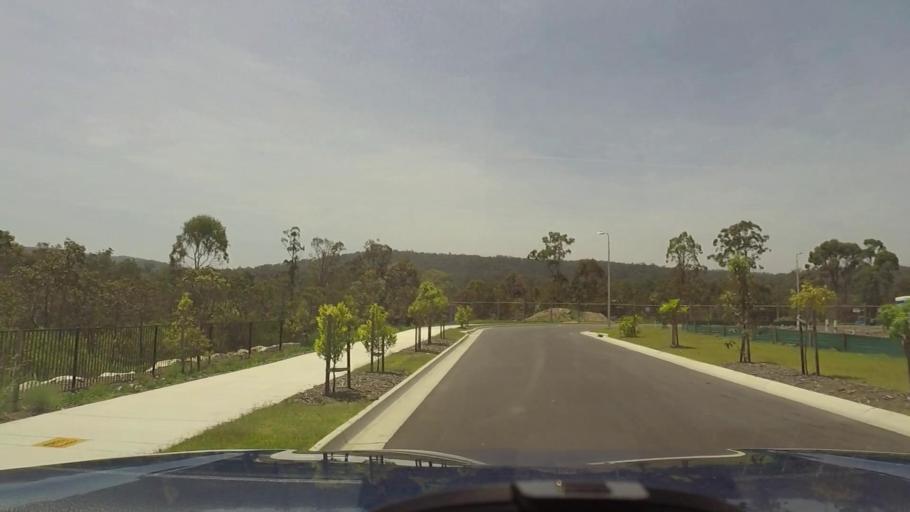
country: AU
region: Queensland
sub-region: Logan
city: Chambers Flat
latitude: -27.8067
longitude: 153.1258
